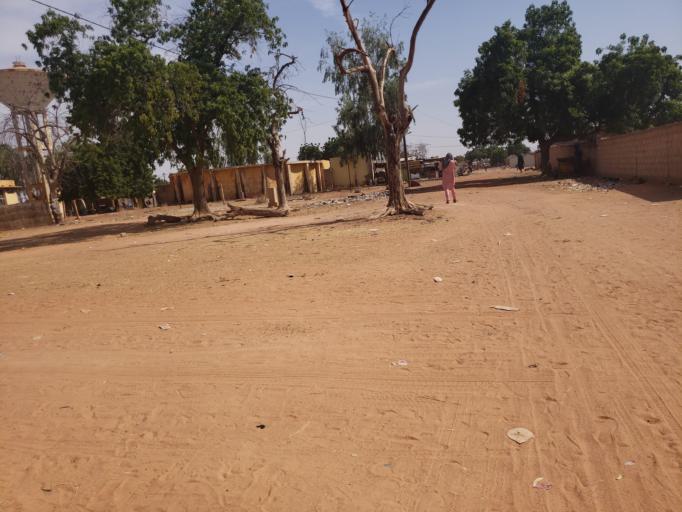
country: SN
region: Matam
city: Ranerou
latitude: 15.2980
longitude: -13.9633
